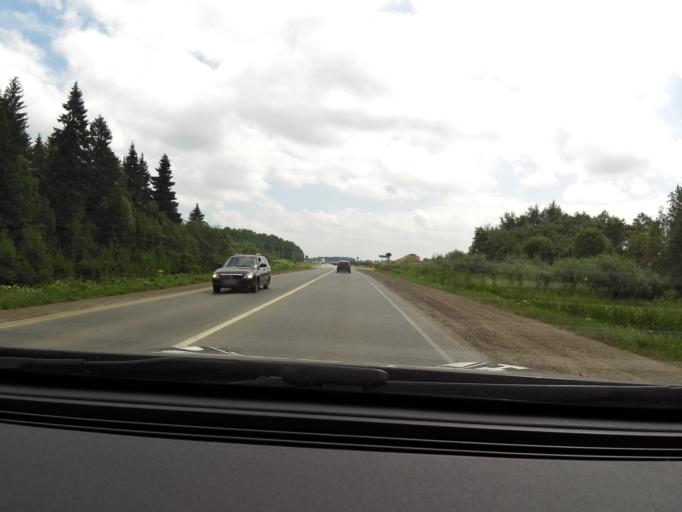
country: RU
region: Perm
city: Bershet'
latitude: 57.6933
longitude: 56.3974
